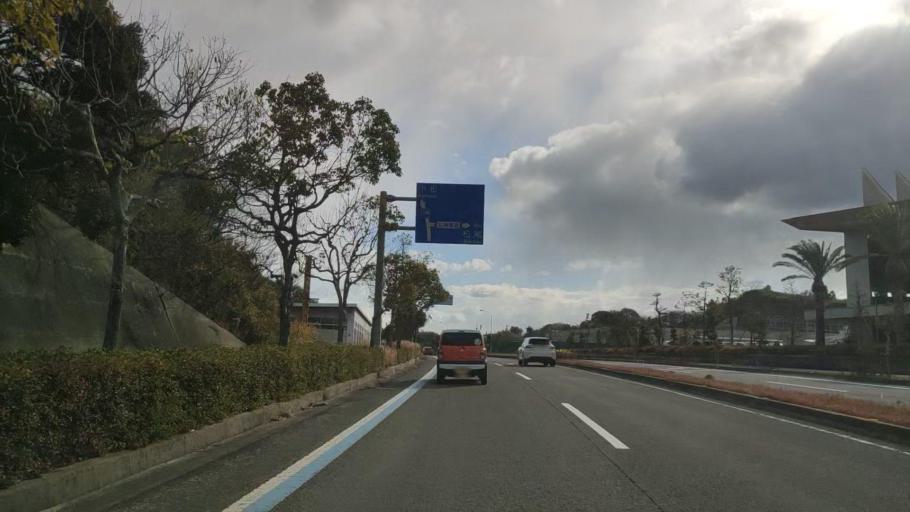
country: JP
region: Ehime
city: Hojo
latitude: 34.0638
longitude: 132.9535
